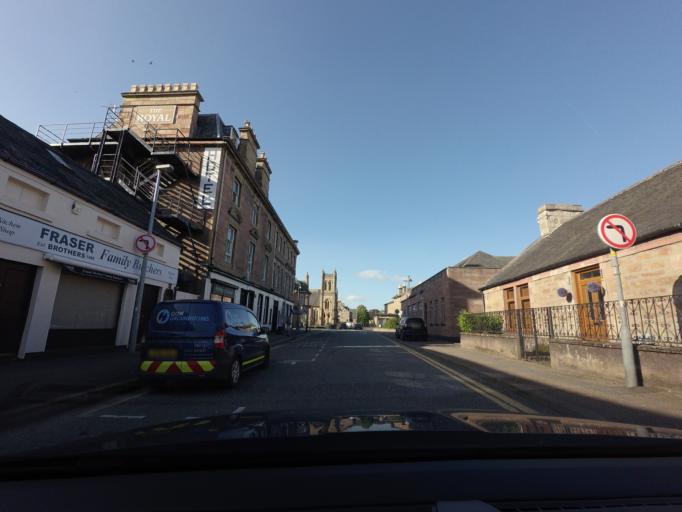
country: GB
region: Scotland
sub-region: Highland
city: Dingwall
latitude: 57.5948
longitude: -4.4257
